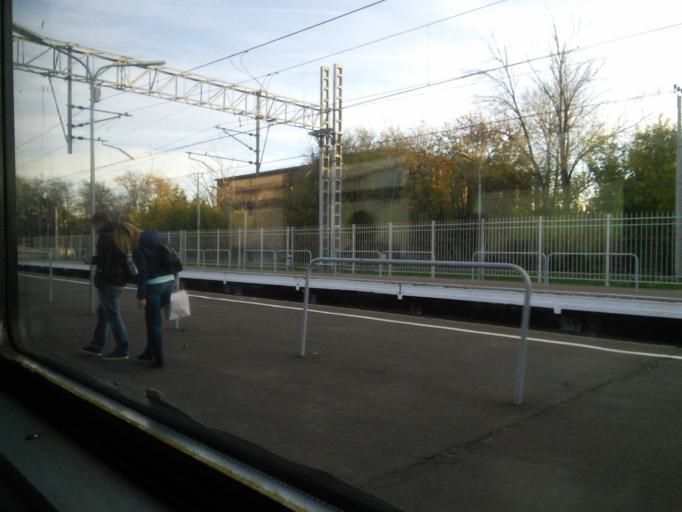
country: RU
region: Moscow
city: Ostankinskiy
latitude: 55.8170
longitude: 37.6039
